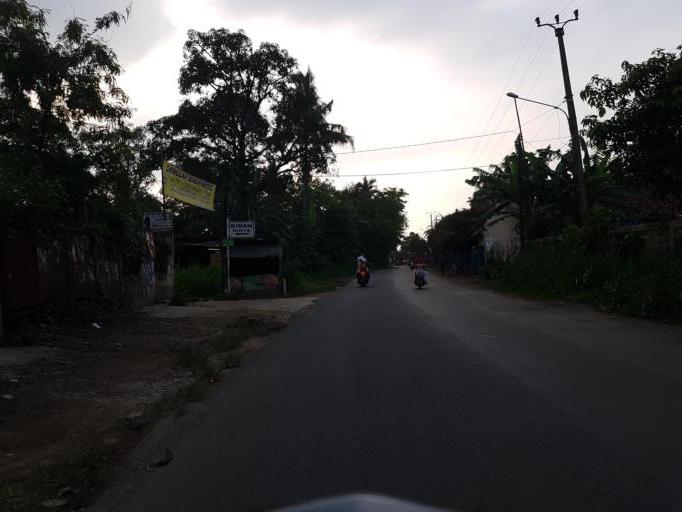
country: ID
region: West Java
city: Parung
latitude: -6.4732
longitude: 106.7202
